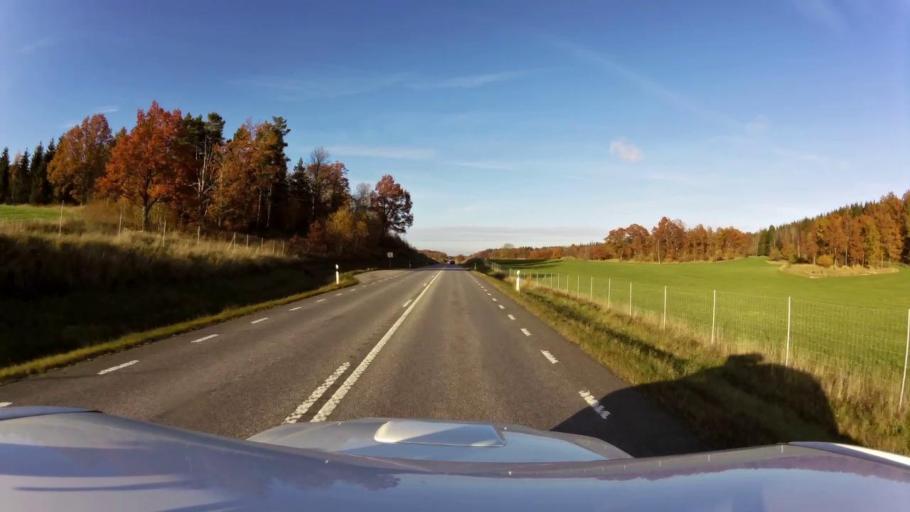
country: SE
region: OEstergoetland
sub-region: Kinda Kommun
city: Rimforsa
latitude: 58.1932
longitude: 15.6669
